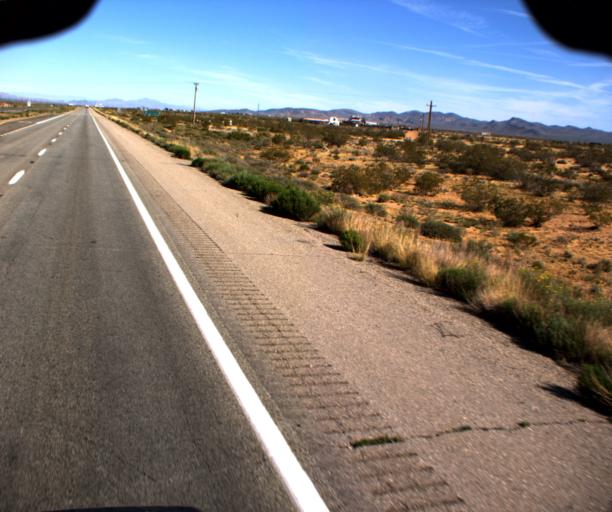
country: US
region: Arizona
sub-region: Mohave County
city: Dolan Springs
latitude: 35.5159
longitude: -114.3427
